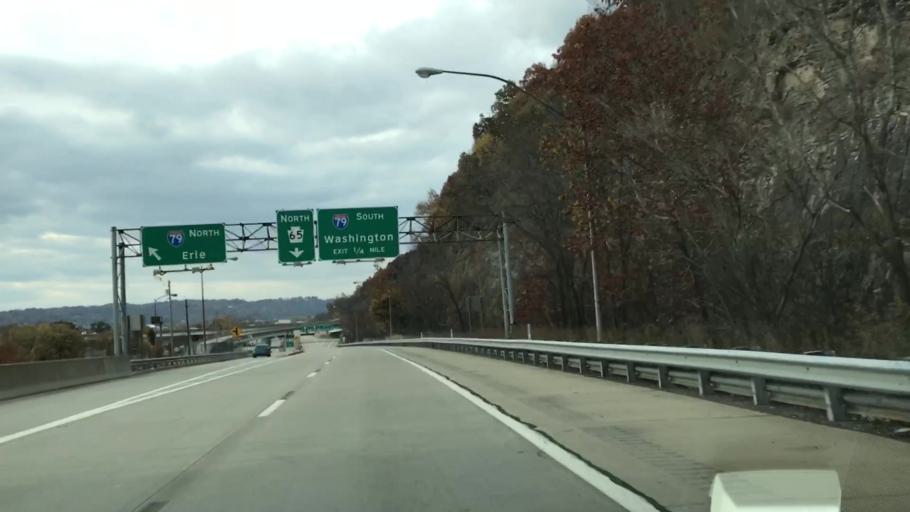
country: US
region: Pennsylvania
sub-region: Allegheny County
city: Emsworth
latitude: 40.5168
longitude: -80.1253
